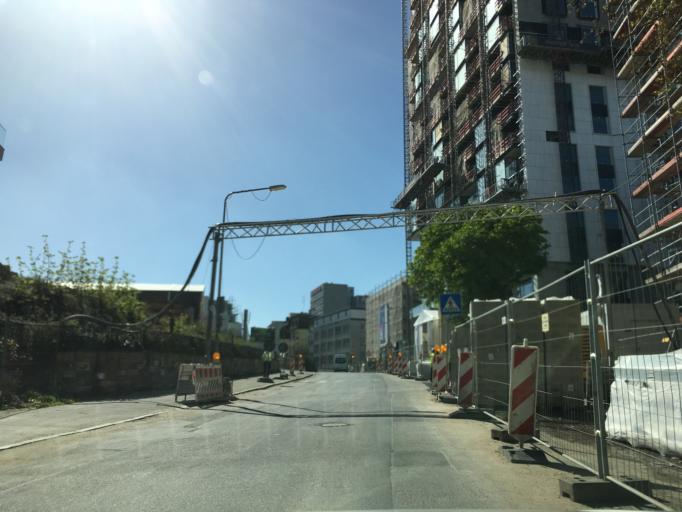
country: DE
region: Hesse
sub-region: Regierungsbezirk Darmstadt
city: Frankfurt am Main
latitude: 50.0979
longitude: 8.6936
